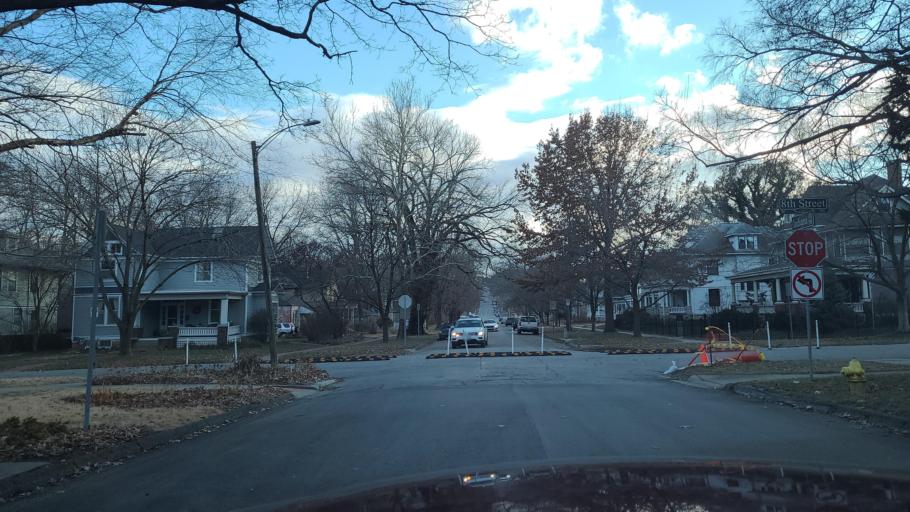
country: US
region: Kansas
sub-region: Douglas County
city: Lawrence
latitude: 38.9697
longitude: -95.2429
